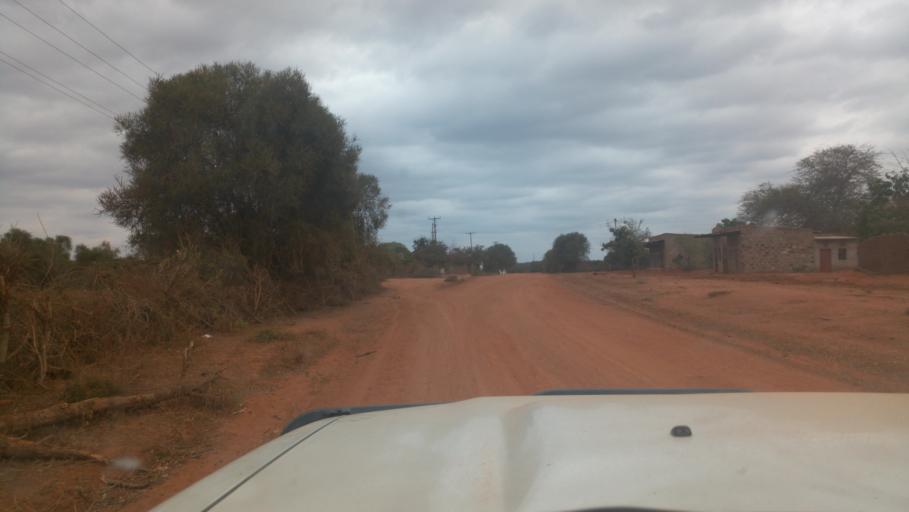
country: KE
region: Makueni
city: Wote
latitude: -1.8995
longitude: 38.0072
